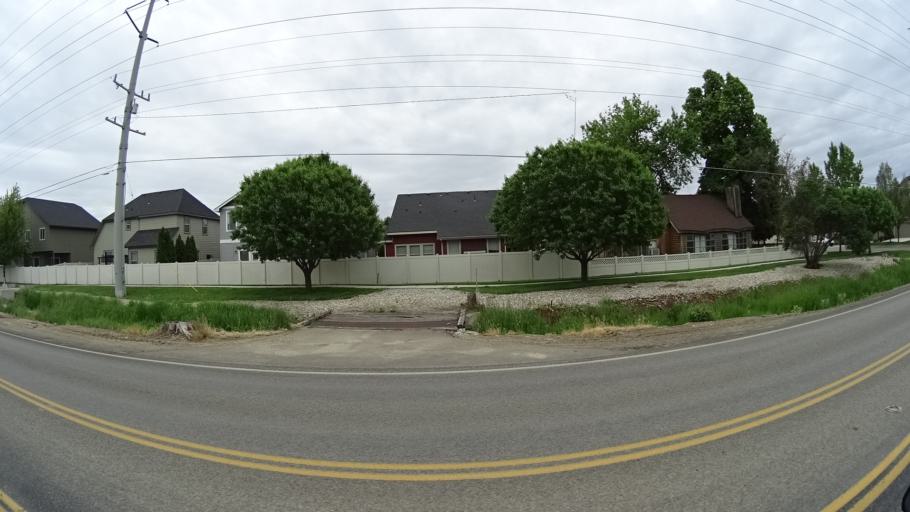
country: US
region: Idaho
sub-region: Ada County
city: Meridian
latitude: 43.6484
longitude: -116.4095
